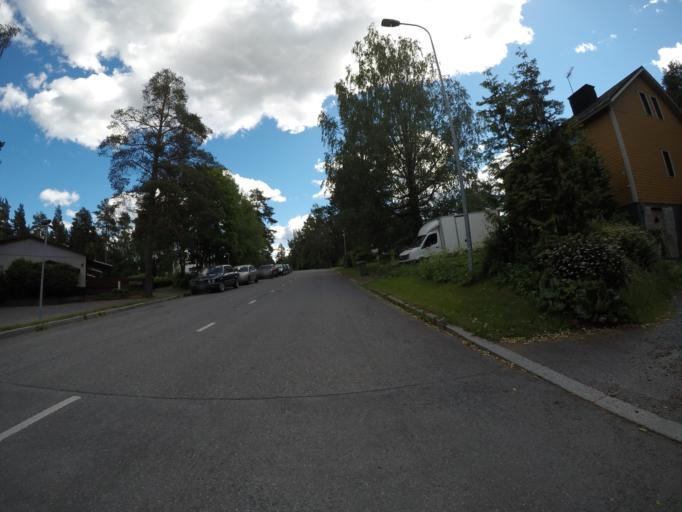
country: FI
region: Haeme
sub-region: Haemeenlinna
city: Haemeenlinna
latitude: 61.0166
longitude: 24.4324
